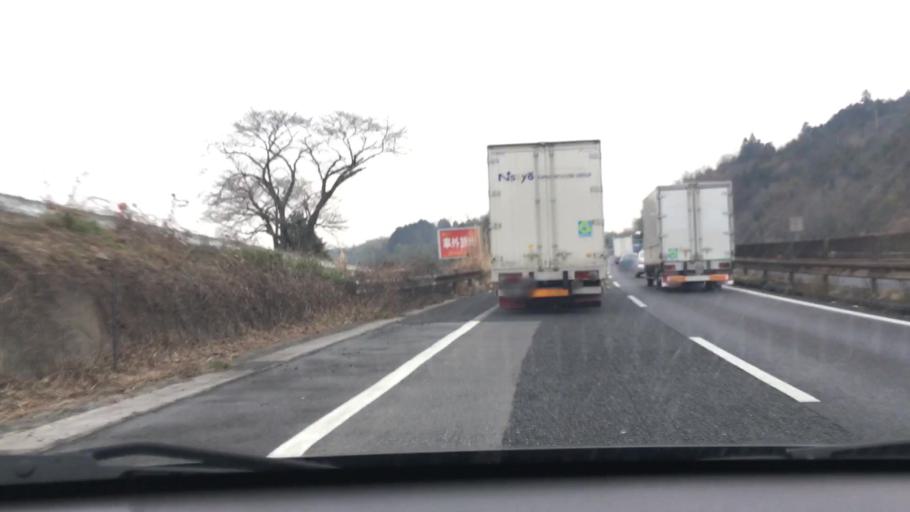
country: JP
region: Mie
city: Ueno-ebisumachi
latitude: 34.7027
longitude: 136.0675
